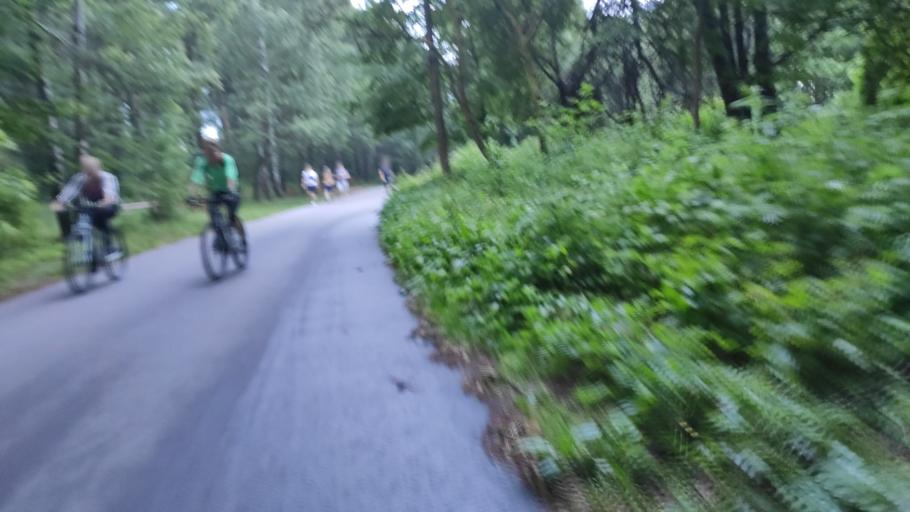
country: BY
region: Minsk
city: Zhdanovichy
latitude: 53.9671
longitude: 27.4384
